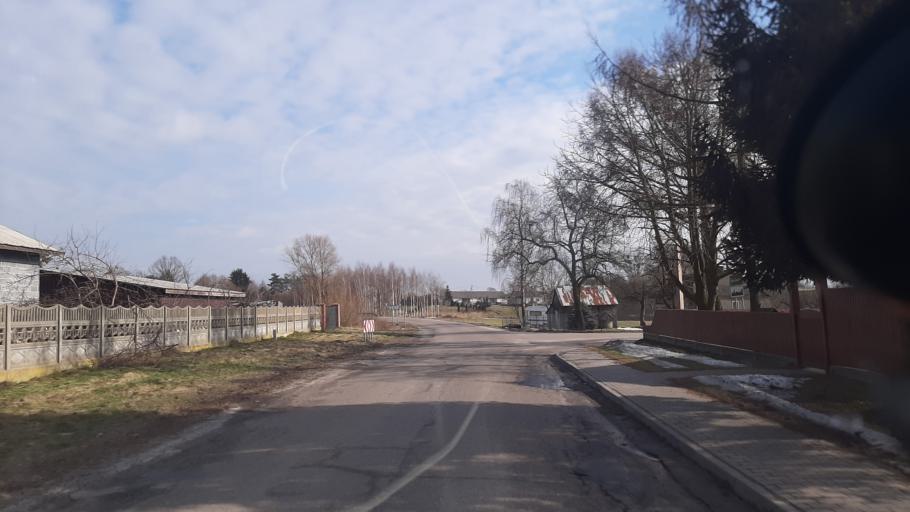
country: PL
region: Lublin Voivodeship
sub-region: Powiat lubartowski
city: Uscimow Stary
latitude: 51.4697
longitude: 22.9545
